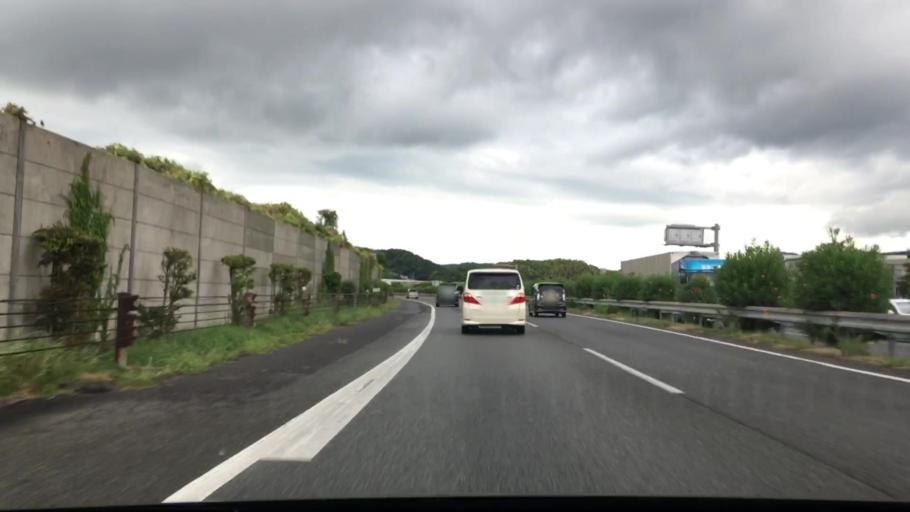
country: JP
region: Fukuoka
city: Sasaguri
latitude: 33.6337
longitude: 130.4908
